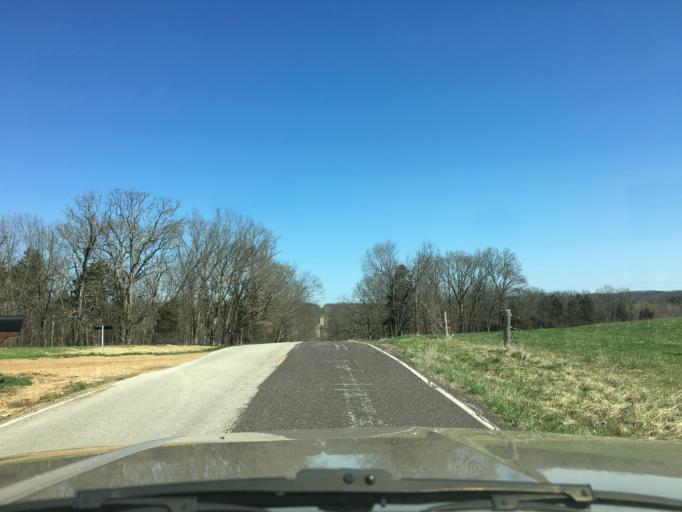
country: US
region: Missouri
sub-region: Franklin County
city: New Haven
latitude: 38.5446
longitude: -91.3302
